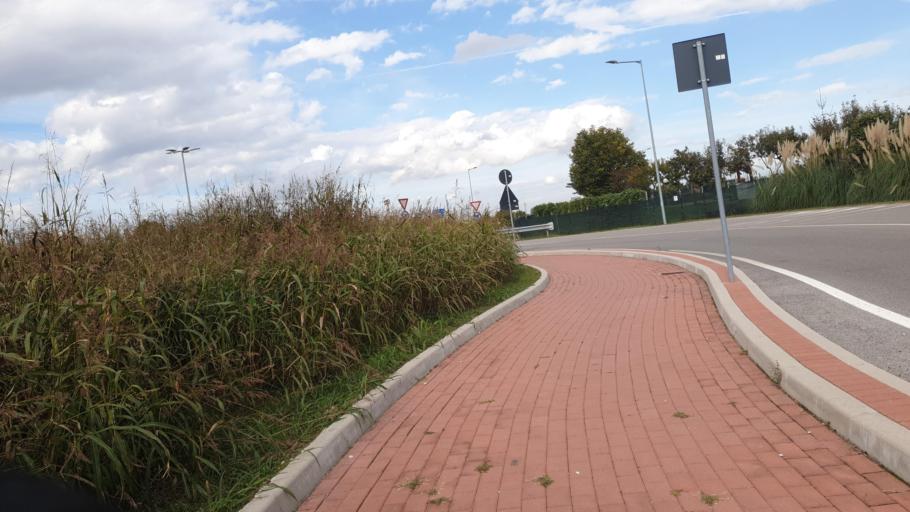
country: IT
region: Veneto
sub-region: Provincia di Padova
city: Campagnola
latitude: 45.2751
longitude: 12.0113
